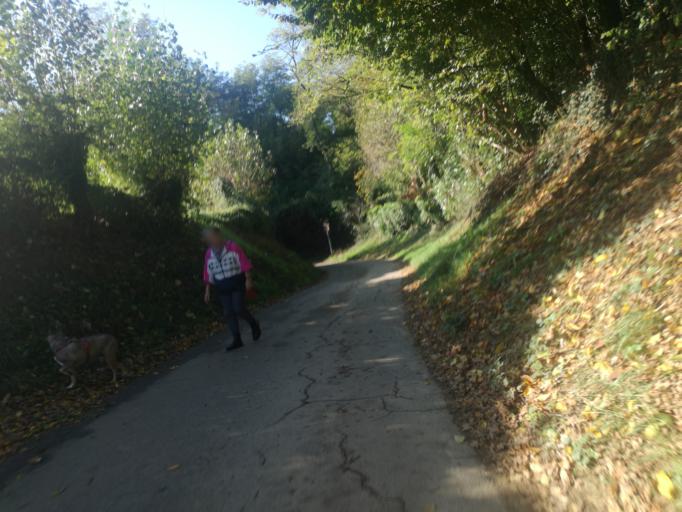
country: IT
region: Lombardy
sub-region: Citta metropolitana di Milano
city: Trezzo sull'Adda
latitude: 45.6183
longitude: 9.5094
